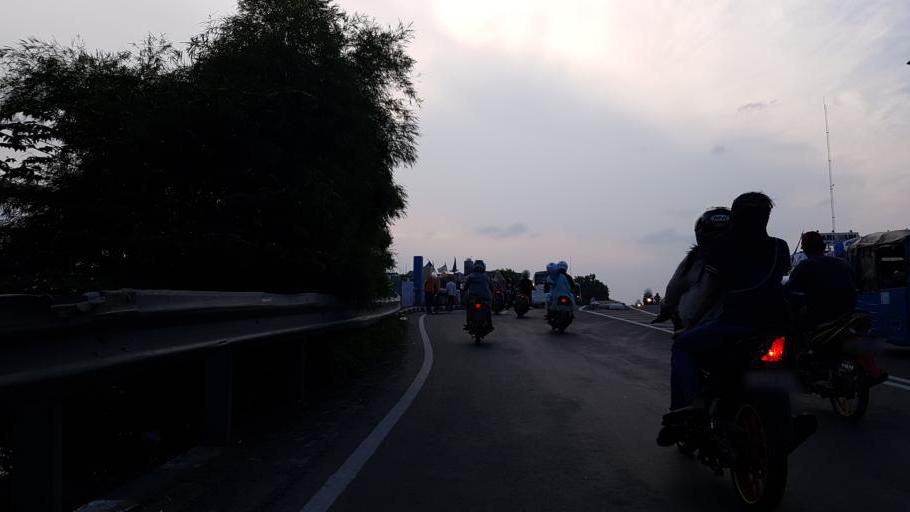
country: ID
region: Jakarta Raya
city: Jakarta
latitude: -6.1388
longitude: 106.7766
